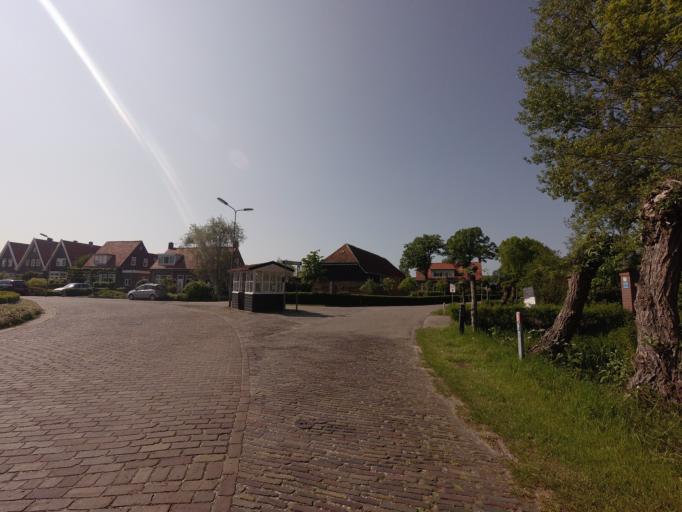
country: NL
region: Zeeland
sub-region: Gemeente Middelburg
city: Middelburg
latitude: 51.5689
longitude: 3.5391
